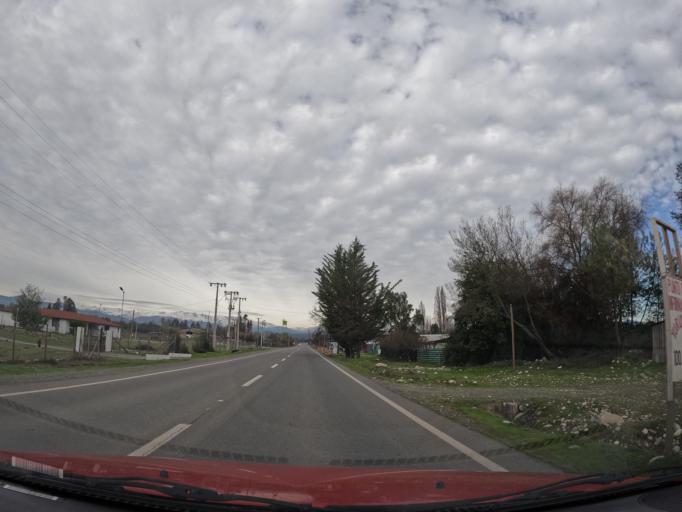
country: CL
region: Maule
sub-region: Provincia de Linares
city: Linares
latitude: -35.9001
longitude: -71.5150
